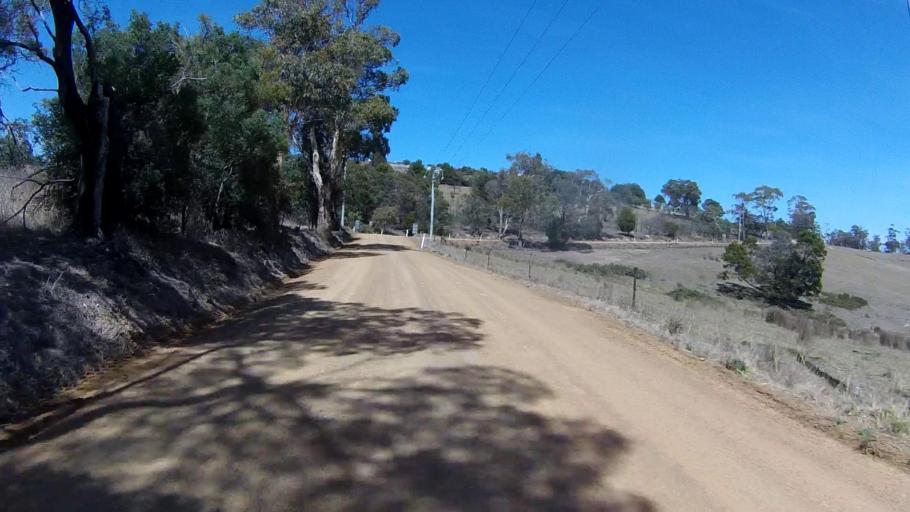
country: AU
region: Tasmania
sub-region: Sorell
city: Sorell
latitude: -42.7803
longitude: 147.6483
